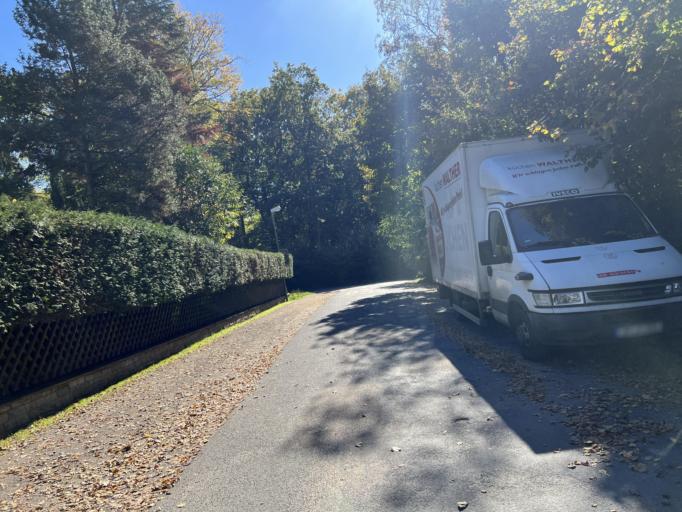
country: DE
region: Hesse
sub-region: Regierungsbezirk Darmstadt
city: Offenbach
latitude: 50.0912
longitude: 8.7897
